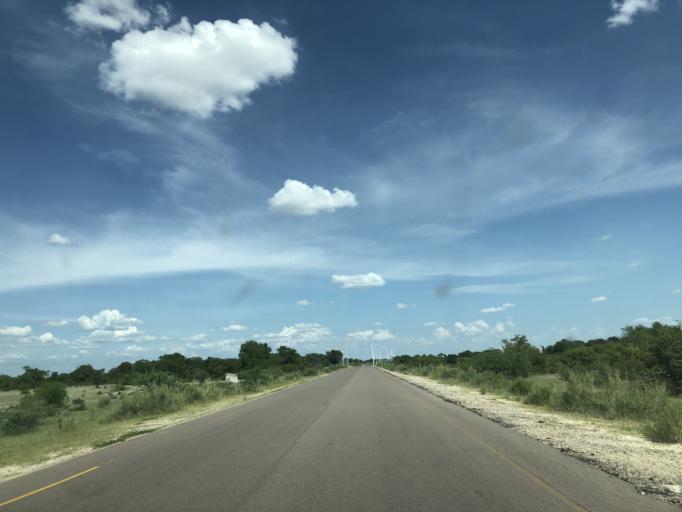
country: AO
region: Cunene
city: Ondjiva
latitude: -17.0051
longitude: 15.6428
